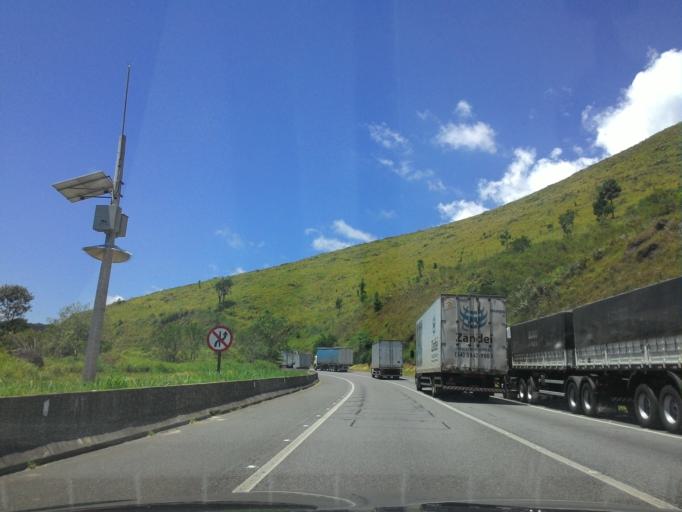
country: BR
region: Sao Paulo
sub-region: Cajati
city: Cajati
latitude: -24.9671
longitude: -48.4723
